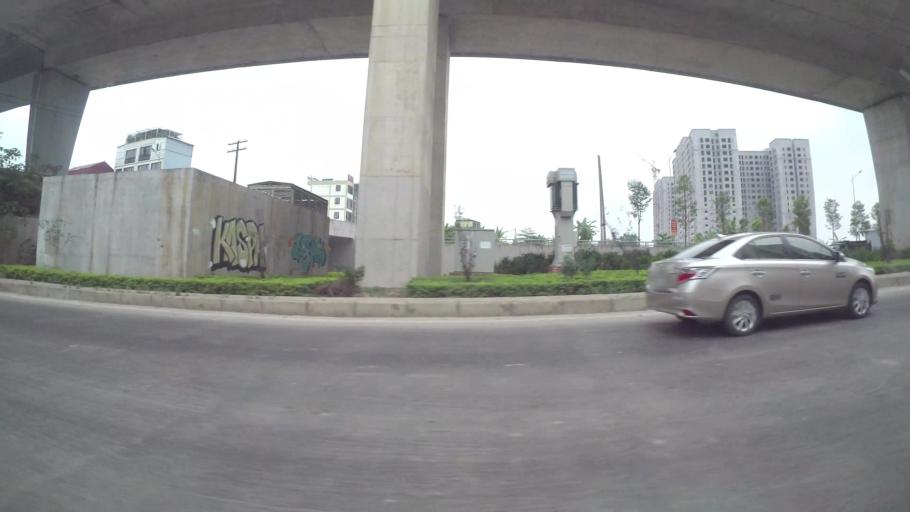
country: VN
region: Ha Noi
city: Hoan Kiem
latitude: 21.0565
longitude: 105.8870
